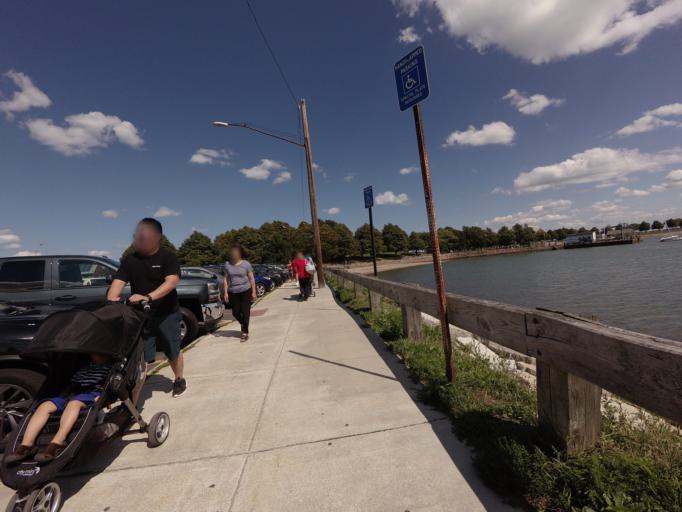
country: US
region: Massachusetts
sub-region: Suffolk County
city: South Boston
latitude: 42.3382
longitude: -71.0142
